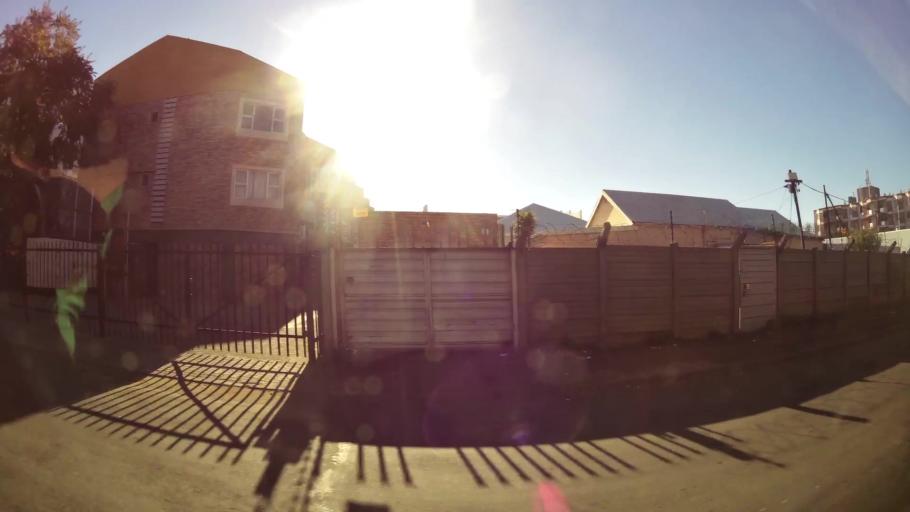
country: ZA
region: Northern Cape
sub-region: Frances Baard District Municipality
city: Kimberley
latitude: -28.7440
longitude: 24.7699
